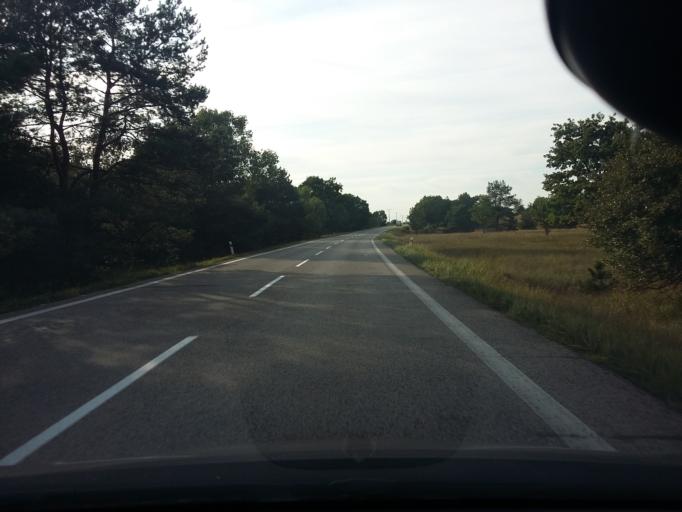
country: SK
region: Bratislavsky
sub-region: Okres Malacky
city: Malacky
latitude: 48.4095
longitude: 17.0710
